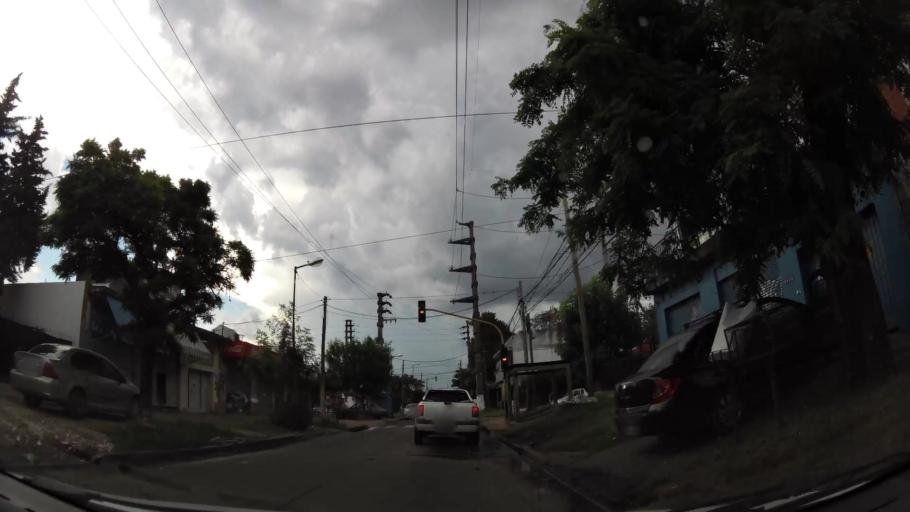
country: AR
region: Buenos Aires
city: Ituzaingo
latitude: -34.6339
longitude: -58.6837
